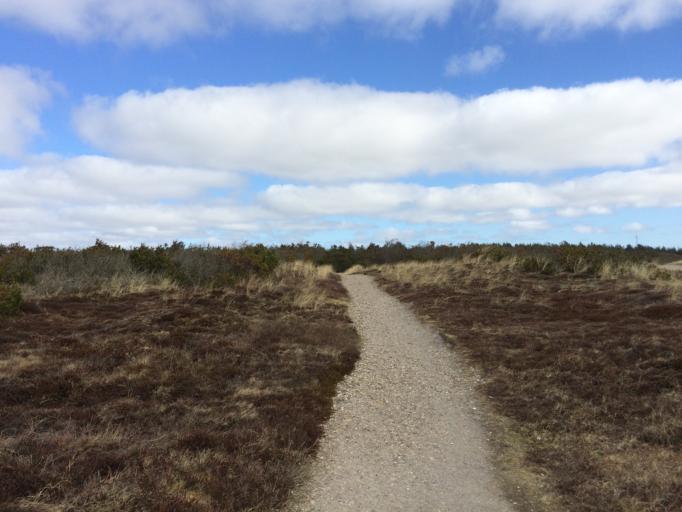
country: DK
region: Central Jutland
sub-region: Holstebro Kommune
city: Ulfborg
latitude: 56.3153
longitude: 8.1283
